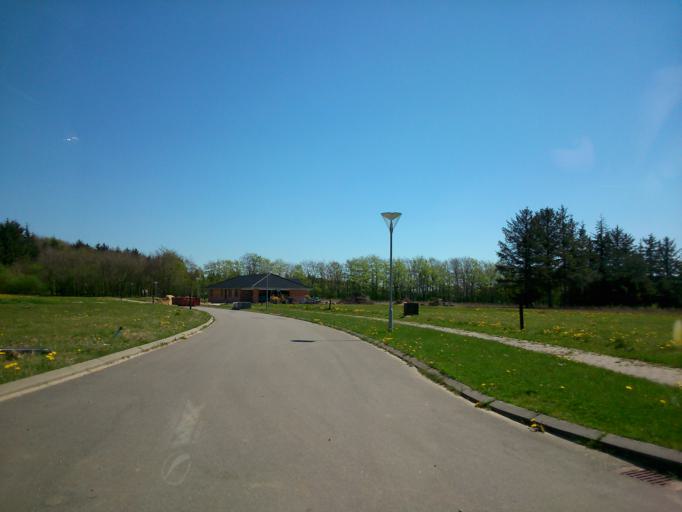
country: DK
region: South Denmark
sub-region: Varde Kommune
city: Olgod
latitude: 55.8150
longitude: 8.6082
